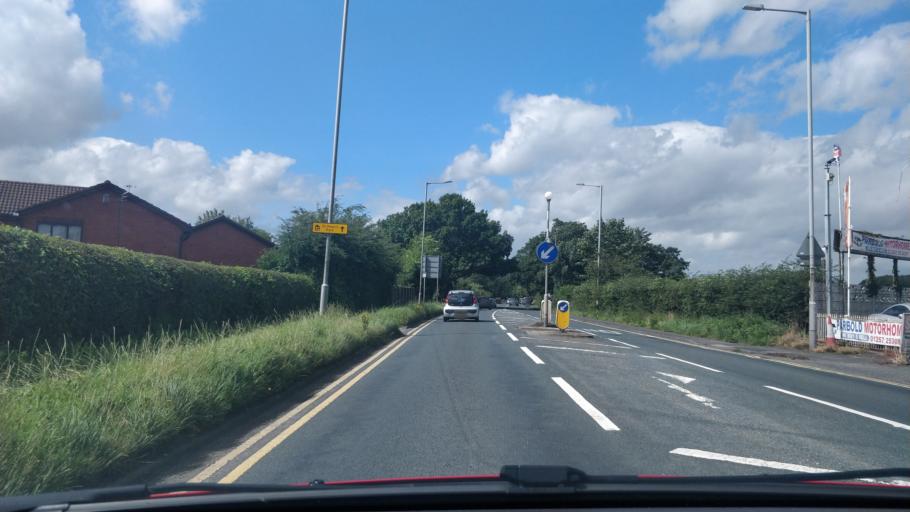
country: GB
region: England
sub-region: Lancashire
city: Appley Bridge
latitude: 53.5921
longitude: -2.7254
